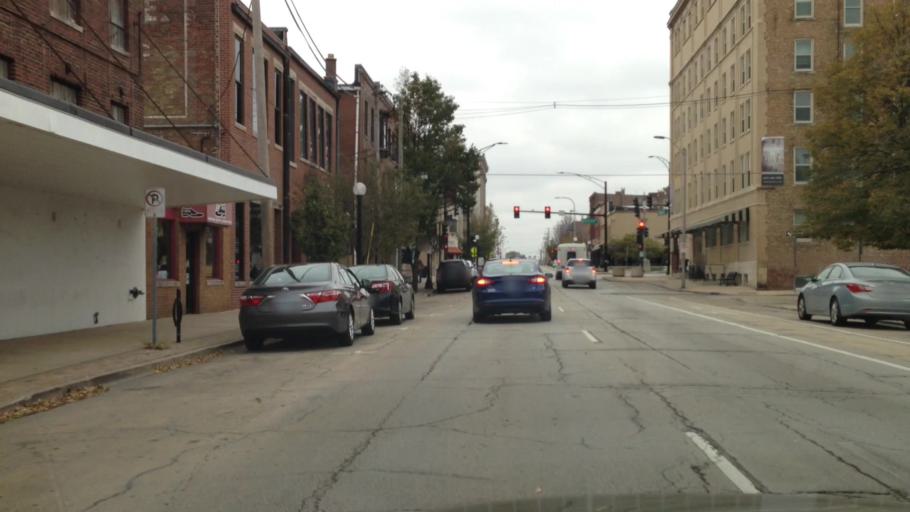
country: US
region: Illinois
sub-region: Champaign County
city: Champaign
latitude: 40.1156
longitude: -88.2430
